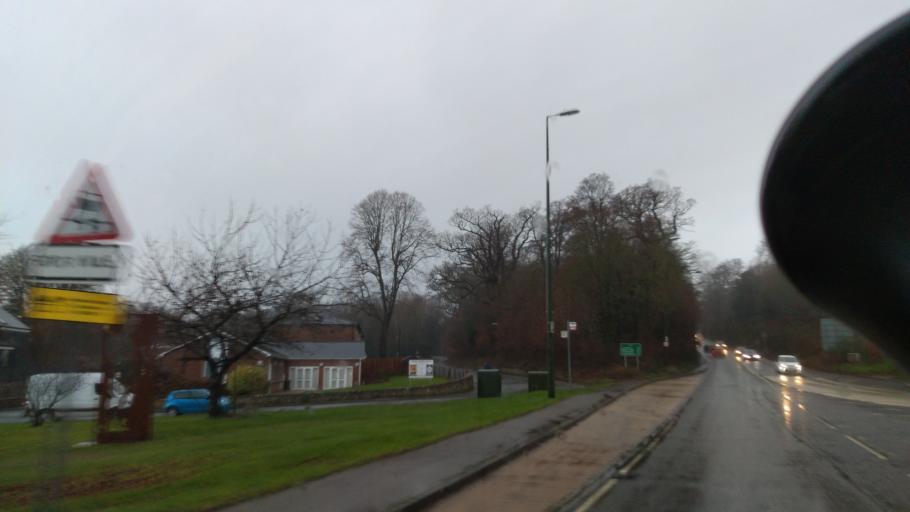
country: GB
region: England
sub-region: West Sussex
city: Arundel
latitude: 50.8525
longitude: -0.5618
